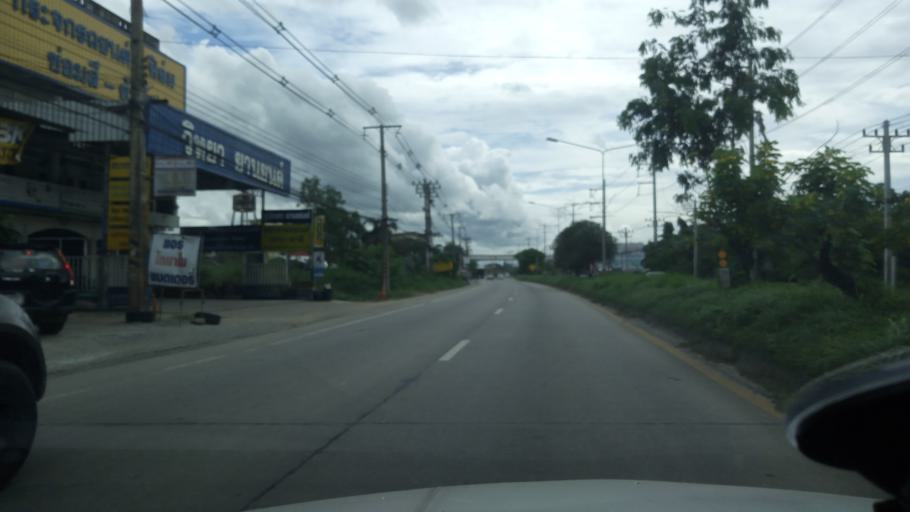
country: TH
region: Chon Buri
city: Phanat Nikhom
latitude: 13.4397
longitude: 101.1449
